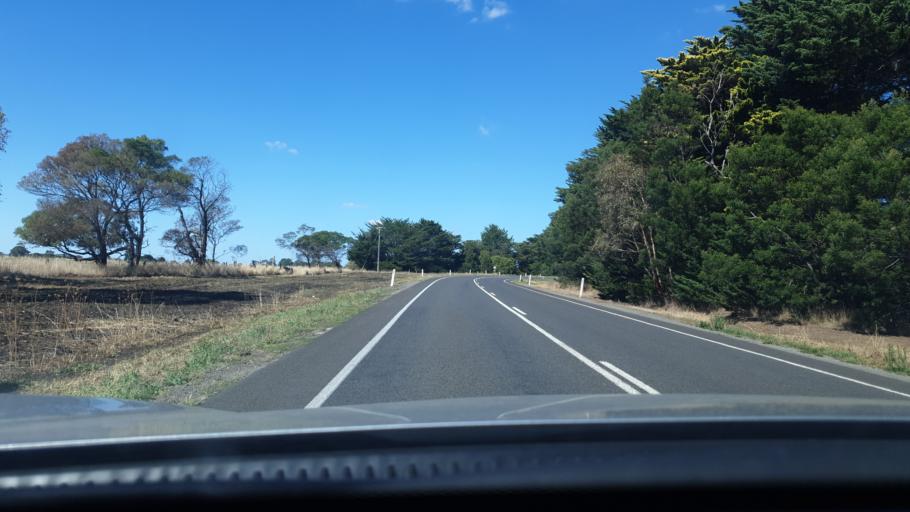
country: AU
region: Victoria
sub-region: Warrnambool
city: Warrnambool
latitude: -38.1779
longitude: 142.4210
